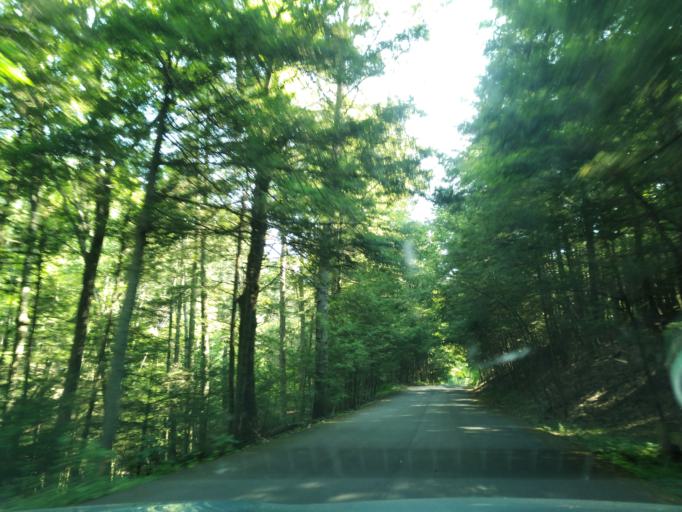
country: US
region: Connecticut
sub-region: New Haven County
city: Southbury
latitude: 41.4279
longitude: -73.2047
